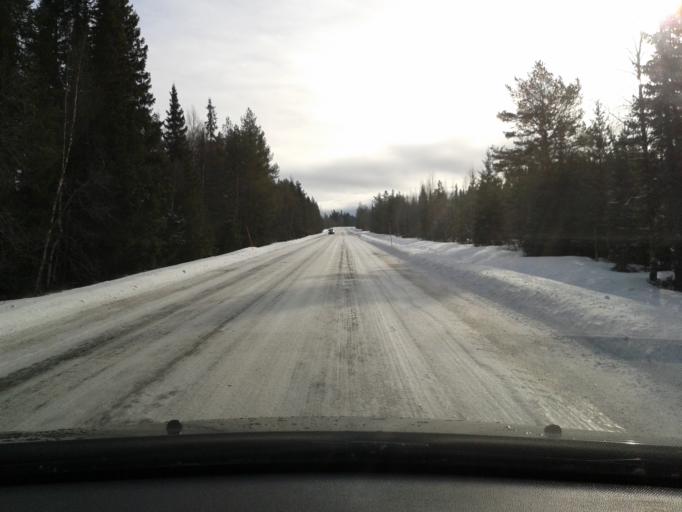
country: SE
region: Vaesterbotten
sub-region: Vilhelmina Kommun
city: Sjoberg
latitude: 64.7326
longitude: 16.2191
